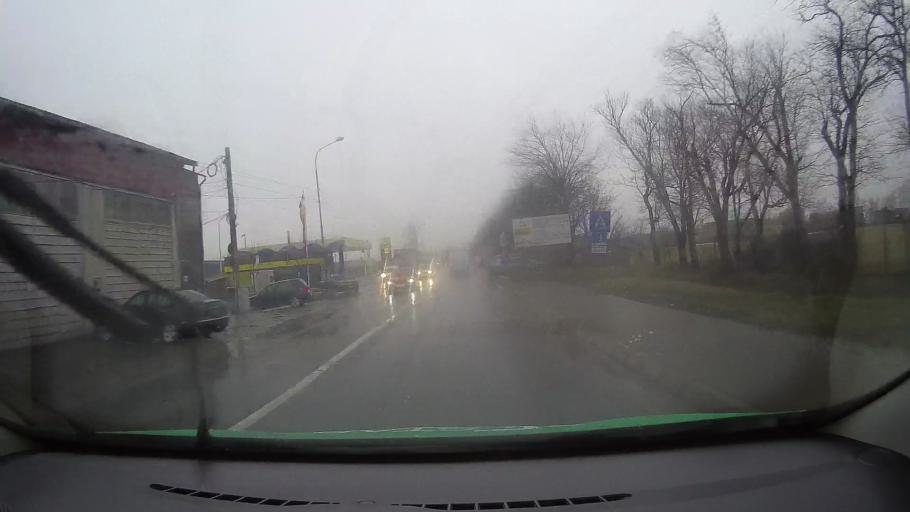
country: RO
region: Sibiu
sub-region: Municipiul Sibiu
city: Sibiu
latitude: 45.8184
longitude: 24.1501
